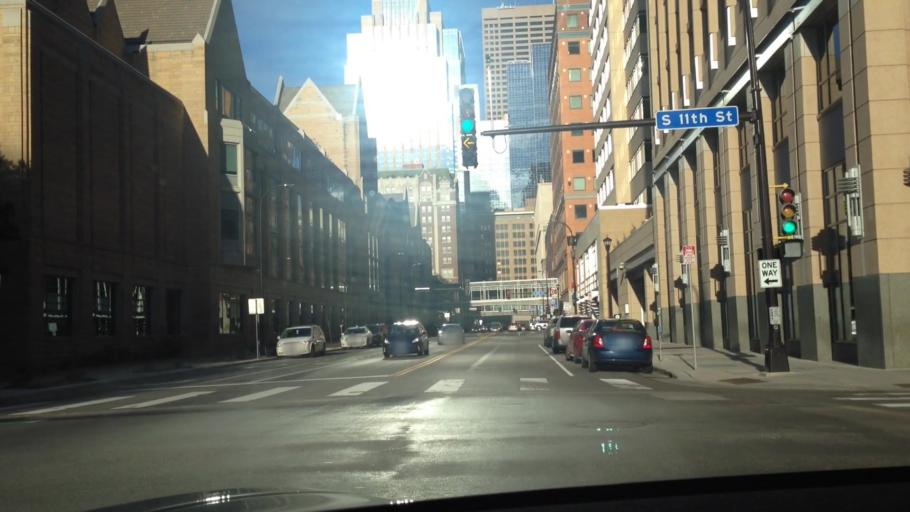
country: US
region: Minnesota
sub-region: Hennepin County
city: Minneapolis
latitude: 44.9735
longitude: -93.2770
